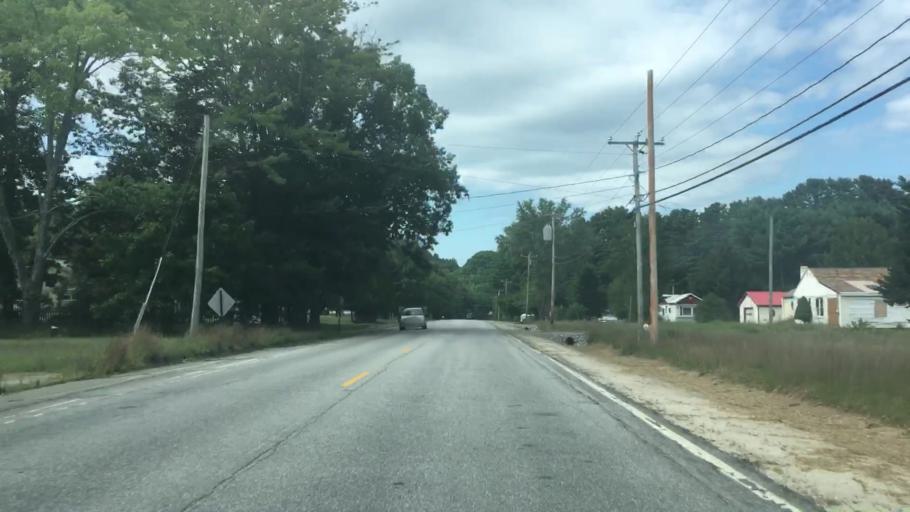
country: US
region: Maine
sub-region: Cumberland County
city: Raymond
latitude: 43.9856
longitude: -70.5190
